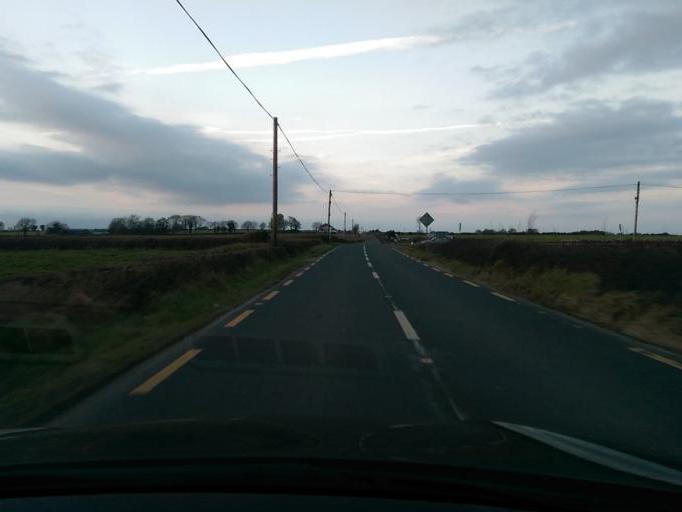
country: IE
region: Connaught
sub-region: County Galway
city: Portumna
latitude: 53.0102
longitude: -8.1254
